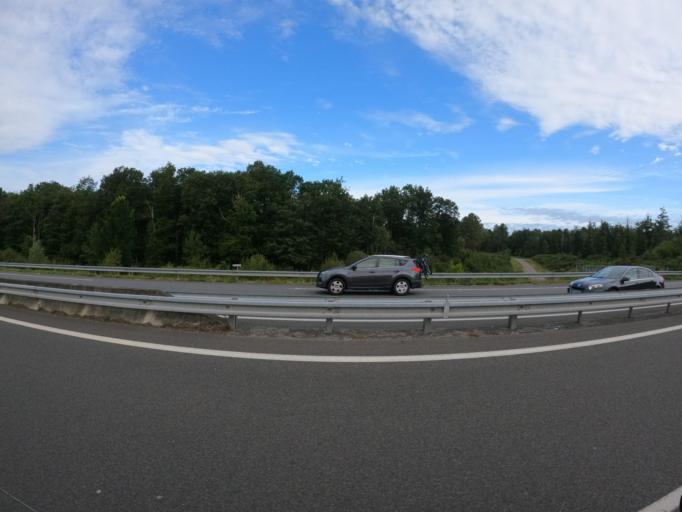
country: FR
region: Centre
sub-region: Departement d'Indre-et-Loire
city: Restigne
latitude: 47.2976
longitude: 0.2894
